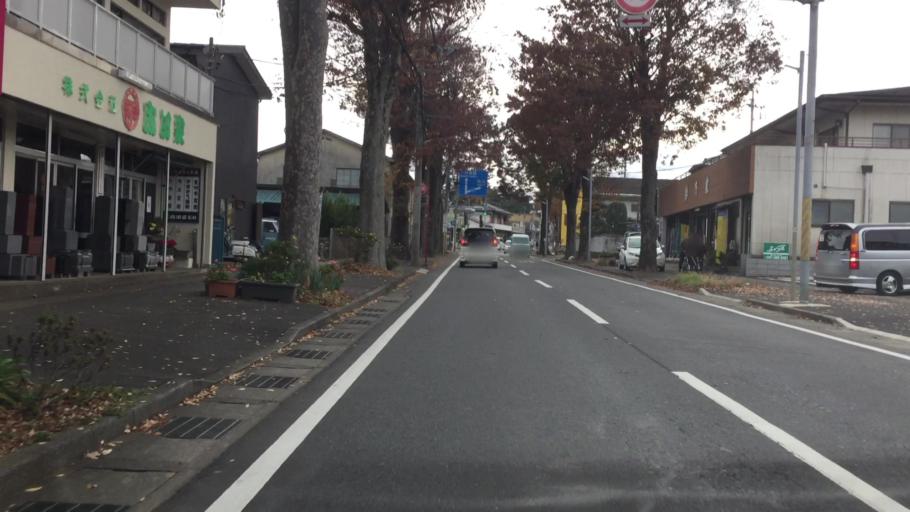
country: JP
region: Chiba
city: Matsudo
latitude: 35.7867
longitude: 139.9448
